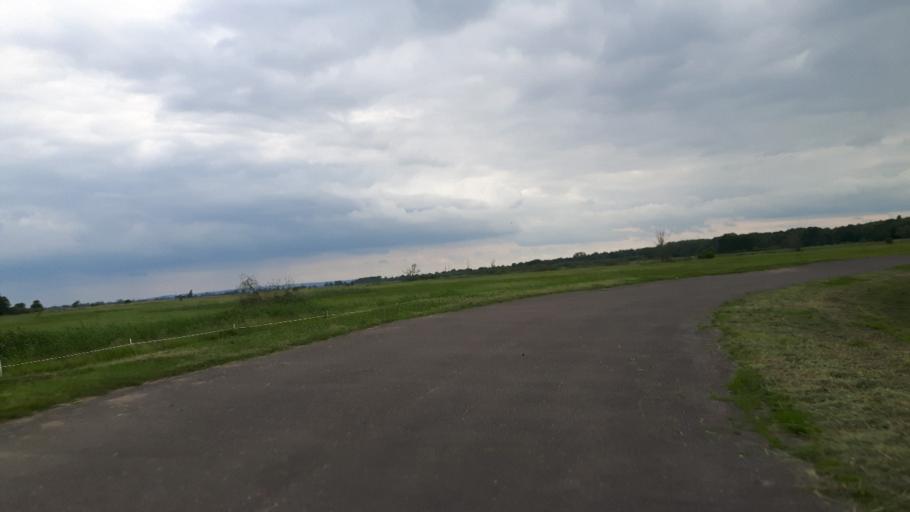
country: PL
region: West Pomeranian Voivodeship
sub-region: Powiat gryfinski
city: Widuchowa
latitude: 53.1328
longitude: 14.3576
